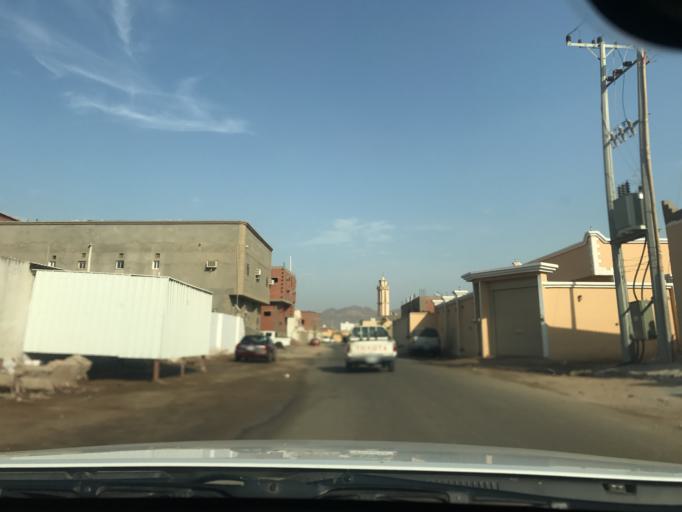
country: SA
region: Makkah
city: Al Jumum
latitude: 21.4412
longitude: 39.5210
